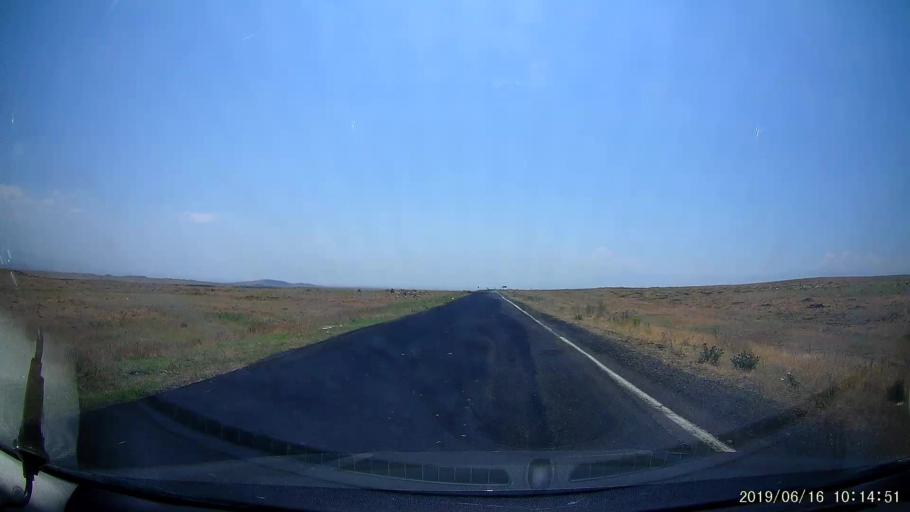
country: TR
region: Igdir
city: Tuzluca
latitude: 40.1813
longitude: 43.6712
